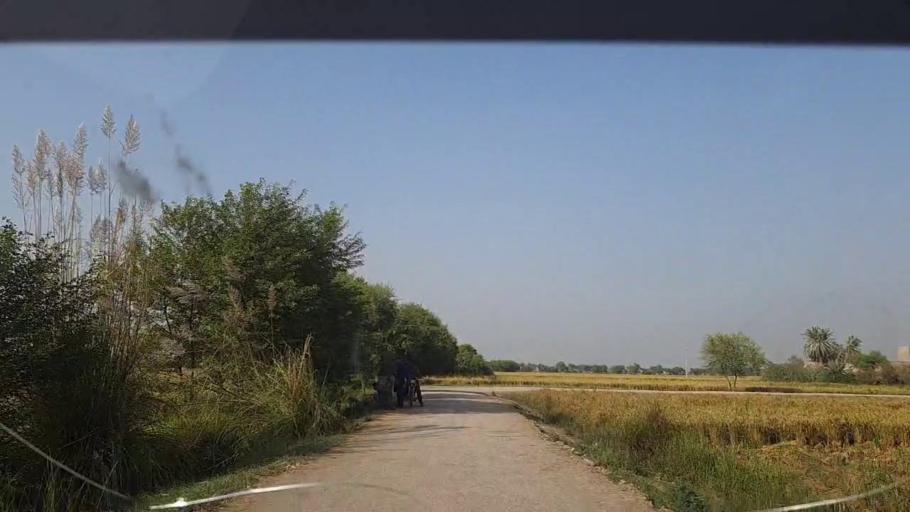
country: PK
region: Sindh
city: Shikarpur
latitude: 28.1167
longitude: 68.5816
